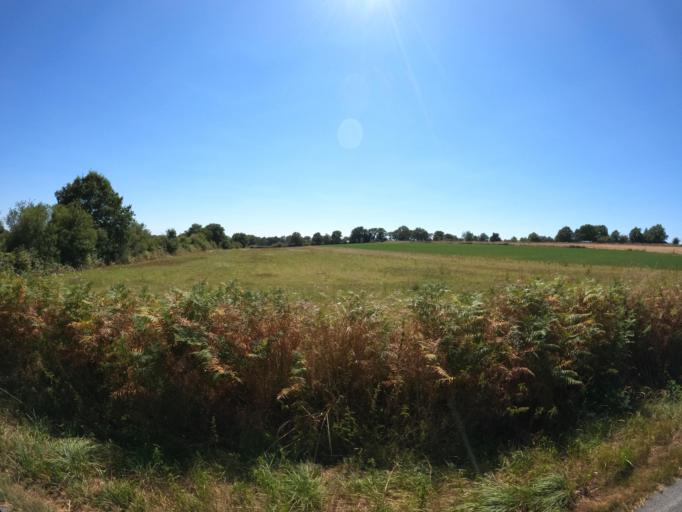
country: FR
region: Pays de la Loire
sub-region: Departement de Maine-et-Loire
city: Saint-Christophe-du-Bois
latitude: 47.0502
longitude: -0.9650
